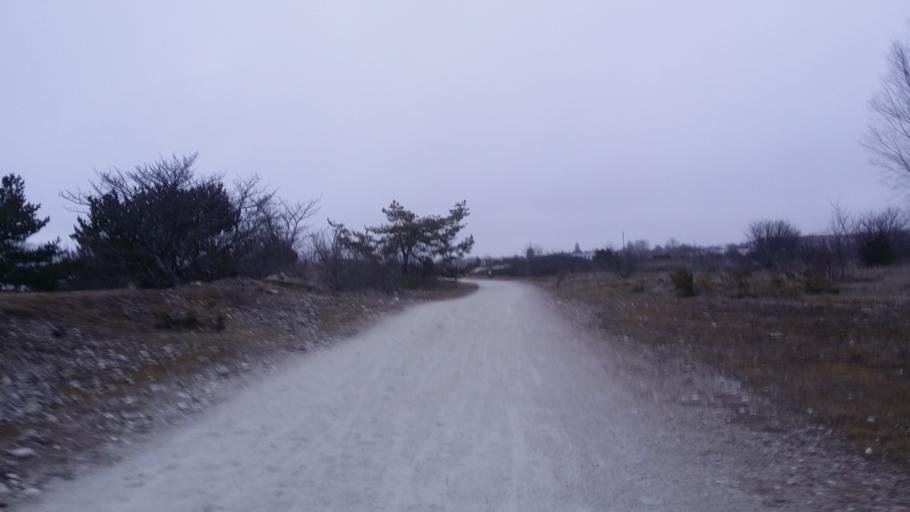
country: SE
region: Gotland
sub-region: Gotland
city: Vibble
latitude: 57.6208
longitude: 18.2669
